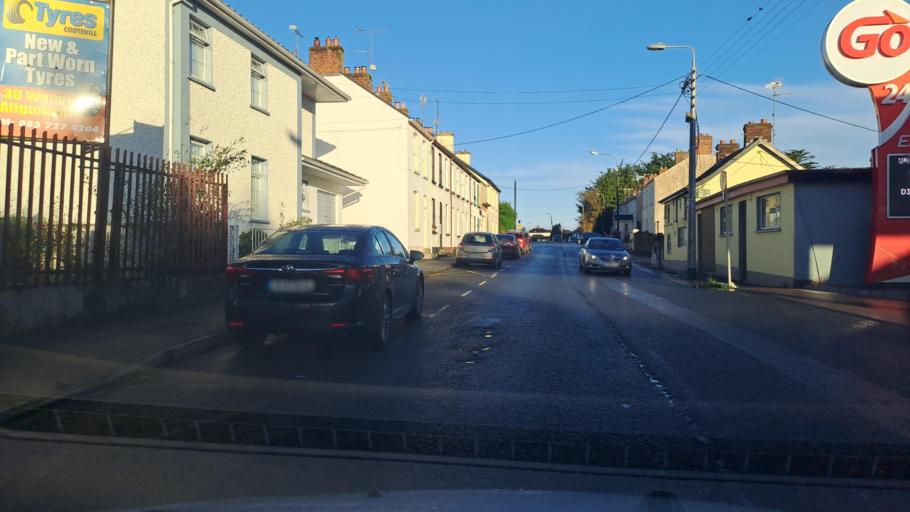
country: IE
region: Ulster
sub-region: An Cabhan
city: Cootehill
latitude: 54.0742
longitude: -7.0852
